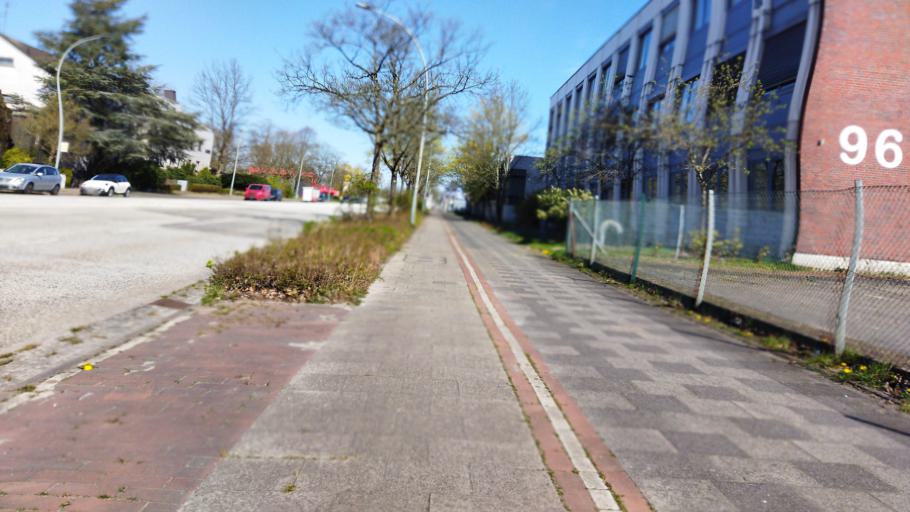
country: DE
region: Bremen
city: Bremerhaven
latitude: 53.5434
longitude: 8.5954
